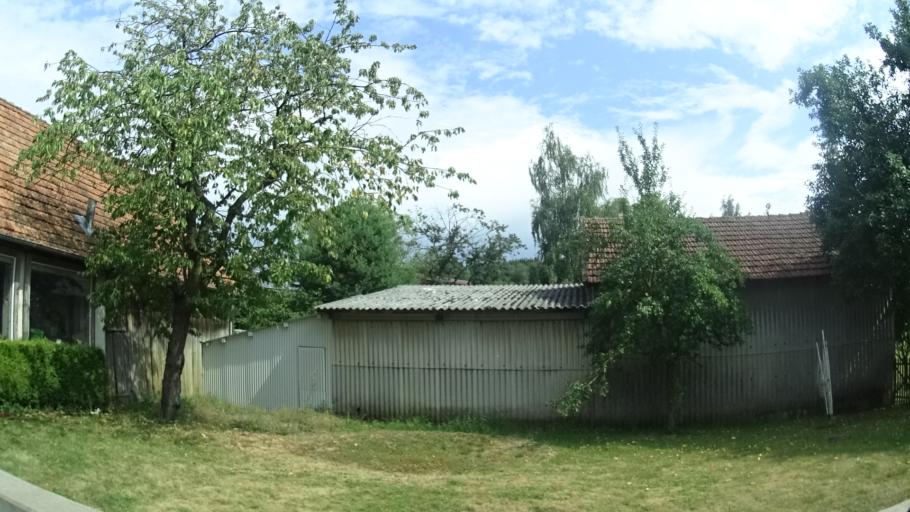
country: DE
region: Hesse
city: Grebenau
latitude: 50.7493
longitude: 9.4847
